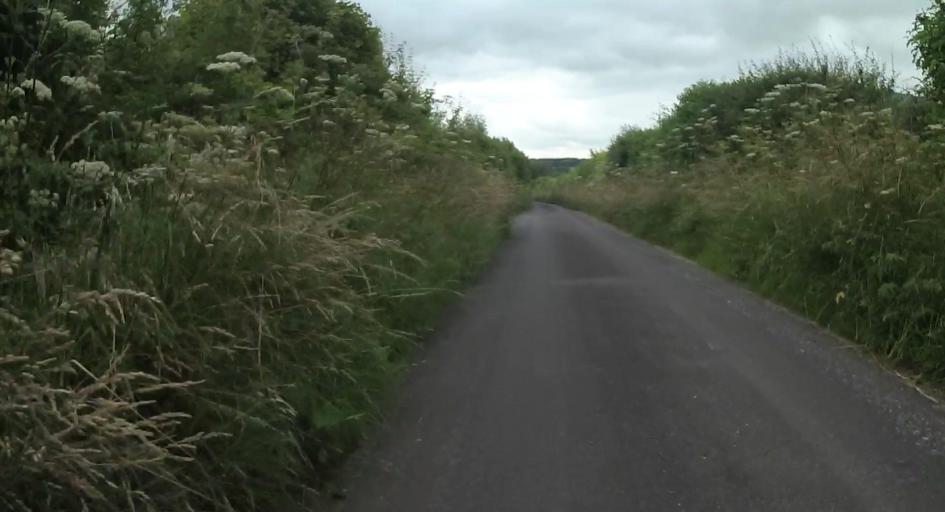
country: GB
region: England
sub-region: Hampshire
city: Kings Worthy
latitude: 51.0980
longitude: -1.2286
